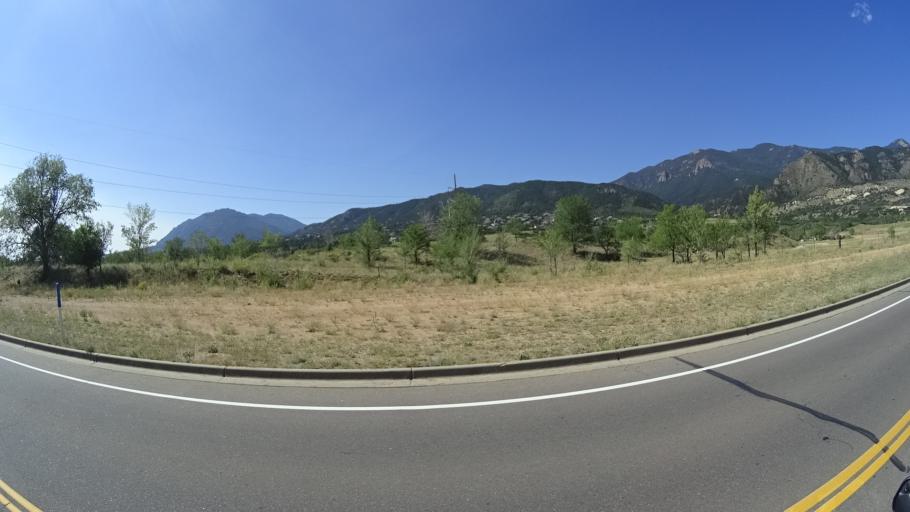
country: US
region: Colorado
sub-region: El Paso County
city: Colorado Springs
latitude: 38.8303
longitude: -104.8687
